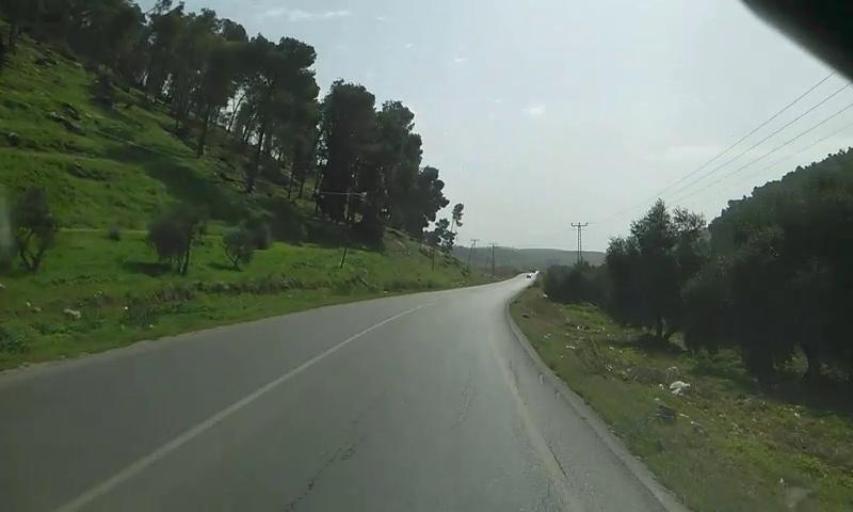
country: PS
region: West Bank
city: Mirkah
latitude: 32.4003
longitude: 35.2246
